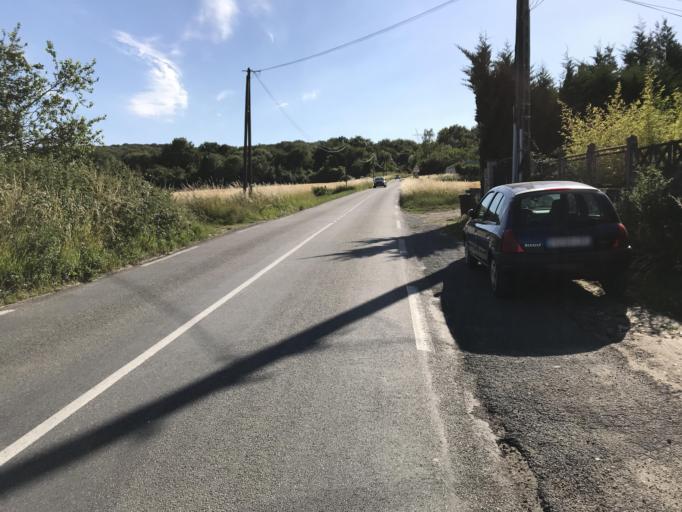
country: FR
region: Ile-de-France
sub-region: Departement de l'Essonne
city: Saulx-les-Chartreux
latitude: 48.6854
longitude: 2.2540
